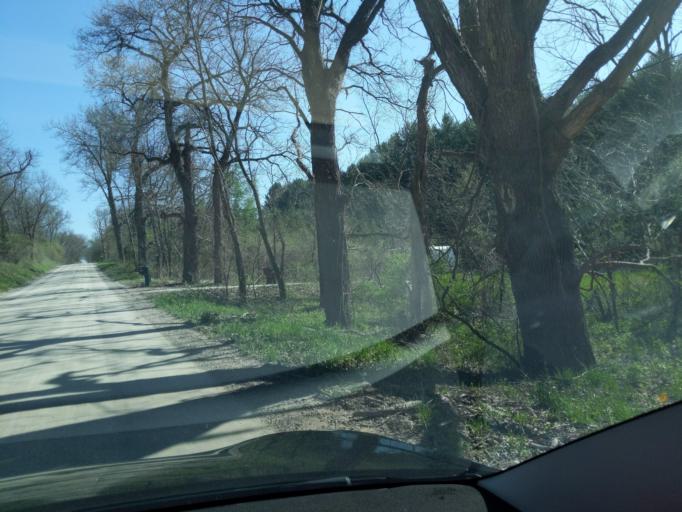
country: US
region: Michigan
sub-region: Washtenaw County
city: Chelsea
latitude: 42.3905
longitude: -84.0837
